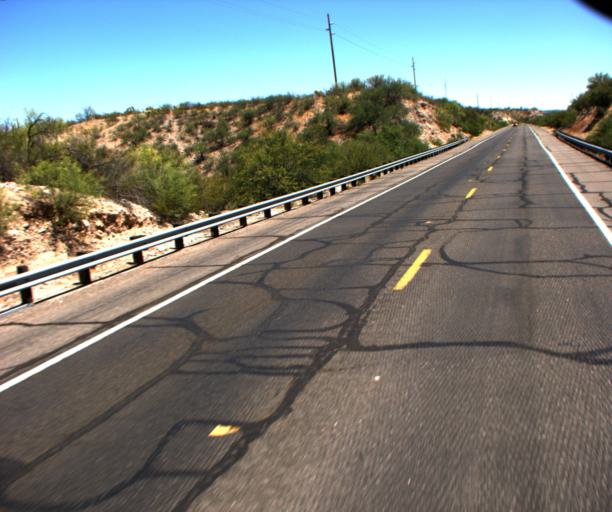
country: US
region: Arizona
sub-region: Pinal County
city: Mammoth
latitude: 32.7574
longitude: -110.6500
